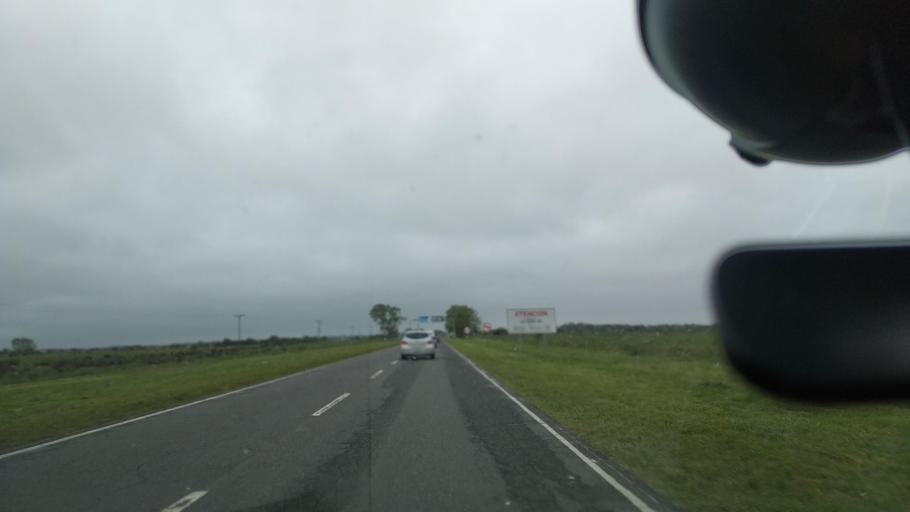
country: AR
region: Buenos Aires
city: Veronica
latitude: -35.5970
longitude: -57.2719
